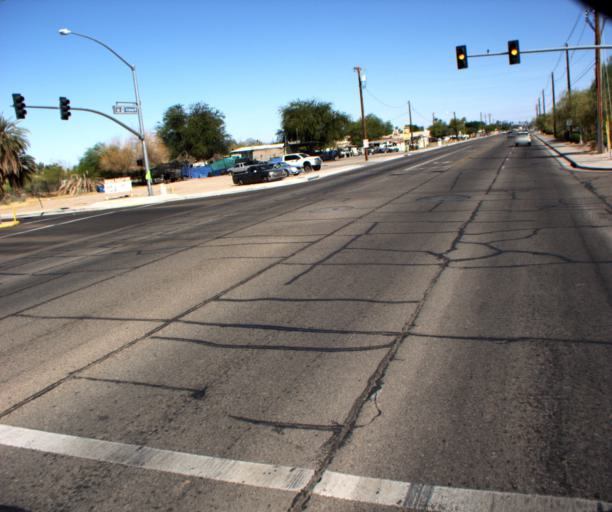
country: US
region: Arizona
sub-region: Yuma County
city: Yuma
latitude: 32.6766
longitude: -114.6502
